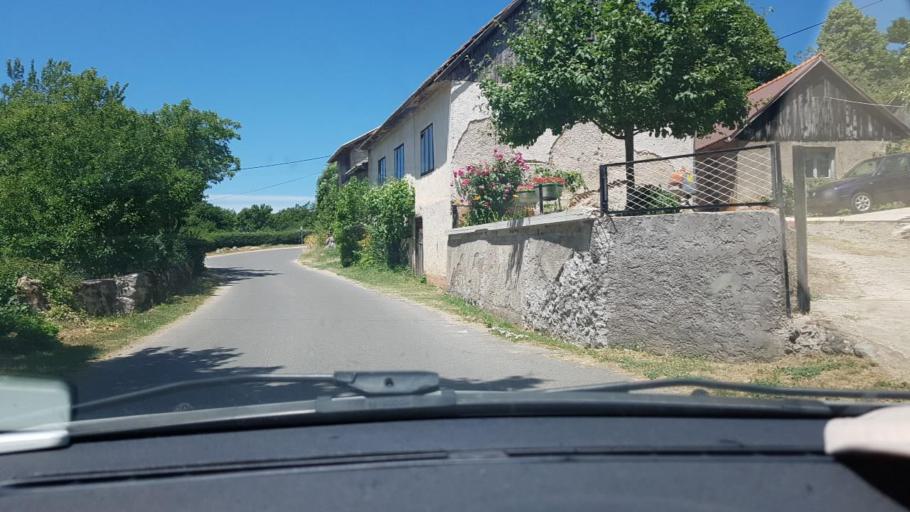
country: HR
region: Licko-Senjska
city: Otocac
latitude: 44.7902
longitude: 15.3684
